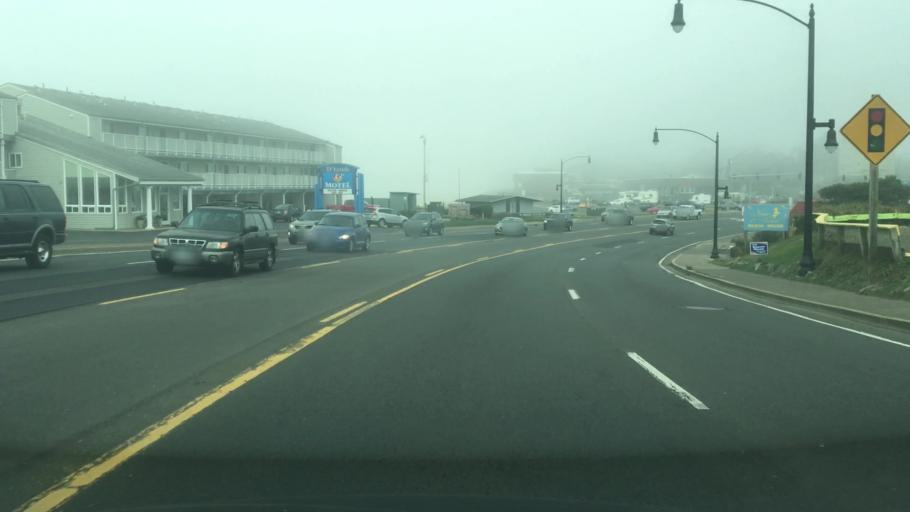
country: US
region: Oregon
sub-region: Lincoln County
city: Lincoln City
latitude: 44.9657
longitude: -124.0178
